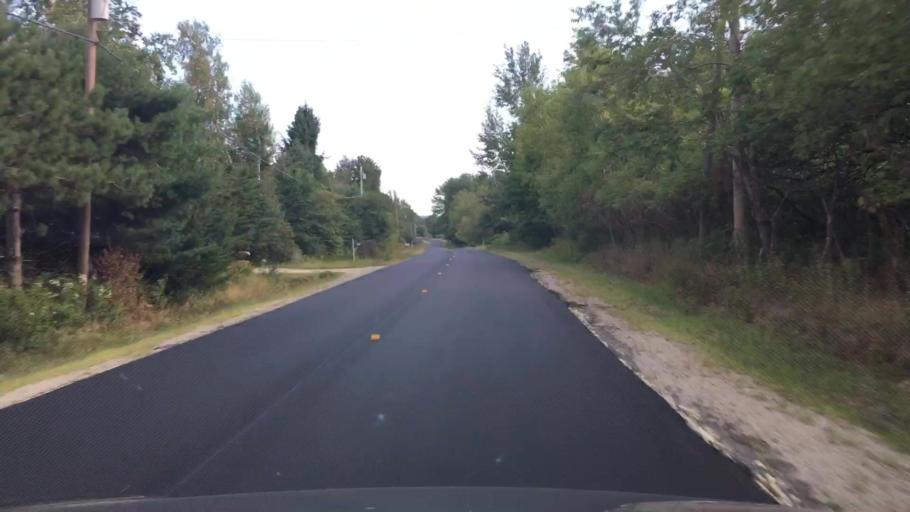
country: US
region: Maine
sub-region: Hancock County
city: Orland
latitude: 44.5525
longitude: -68.6213
